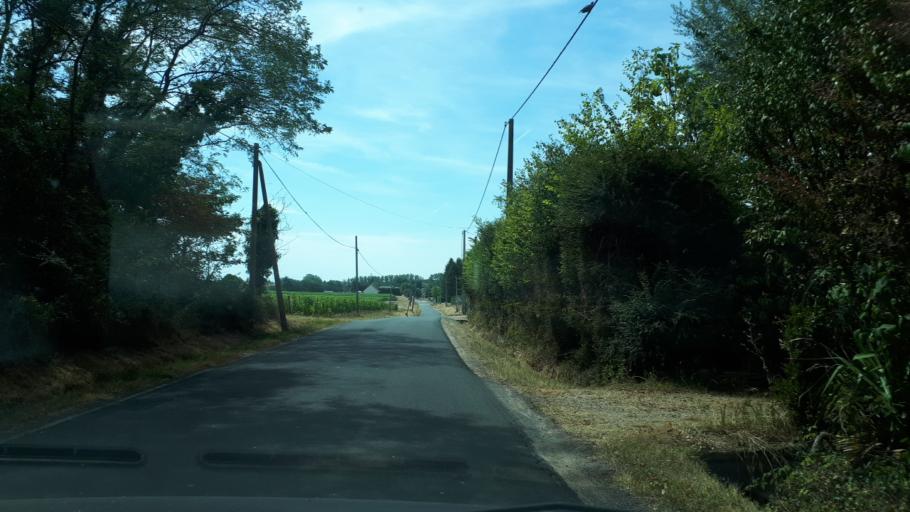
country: FR
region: Centre
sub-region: Departement du Loir-et-Cher
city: Contres
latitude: 47.3980
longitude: 1.3790
